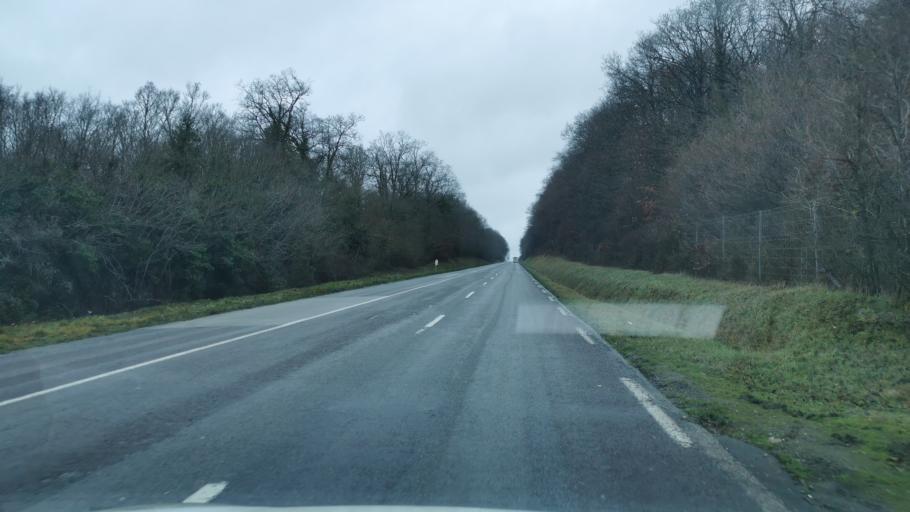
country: FR
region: Haute-Normandie
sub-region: Departement de l'Eure
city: Normanville
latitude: 49.0717
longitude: 1.1752
